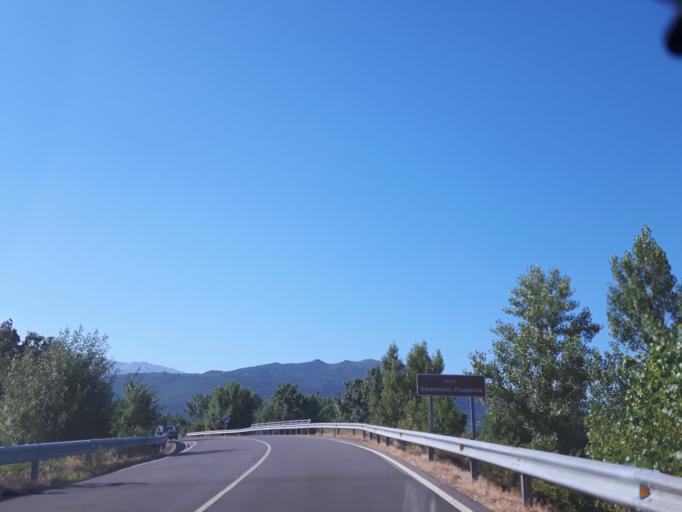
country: ES
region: Castille and Leon
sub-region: Provincia de Salamanca
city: Navalmoral de Bejar
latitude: 40.4079
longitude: -5.8007
